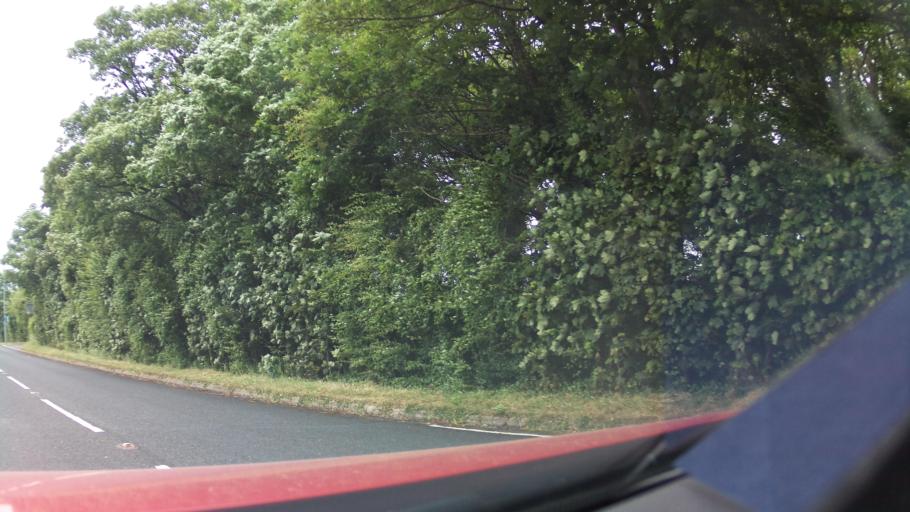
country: GB
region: Wales
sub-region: Vale of Glamorgan
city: Penarth
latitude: 51.4121
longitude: -3.1849
